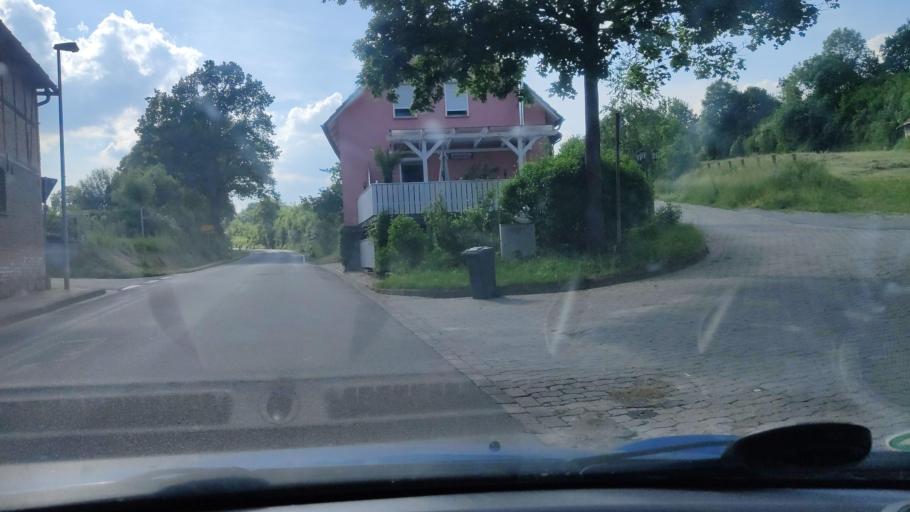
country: DE
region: Lower Saxony
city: Moringen
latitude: 51.7083
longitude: 9.8216
